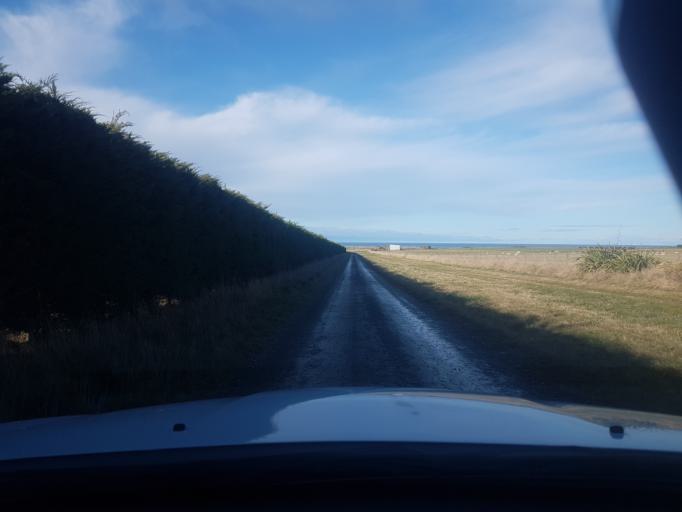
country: NZ
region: Canterbury
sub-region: Timaru District
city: Timaru
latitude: -44.4662
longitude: 171.2277
